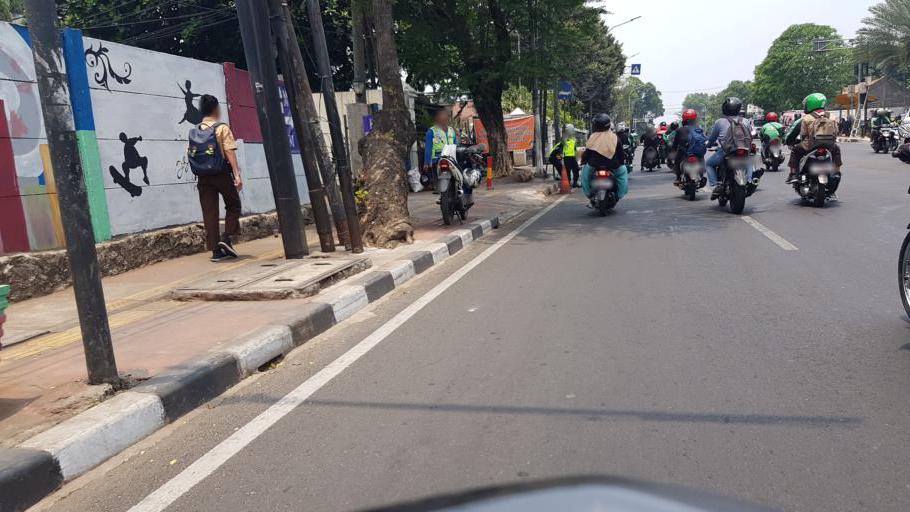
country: ID
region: Jakarta Raya
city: Jakarta
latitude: -6.3042
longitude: 106.8616
